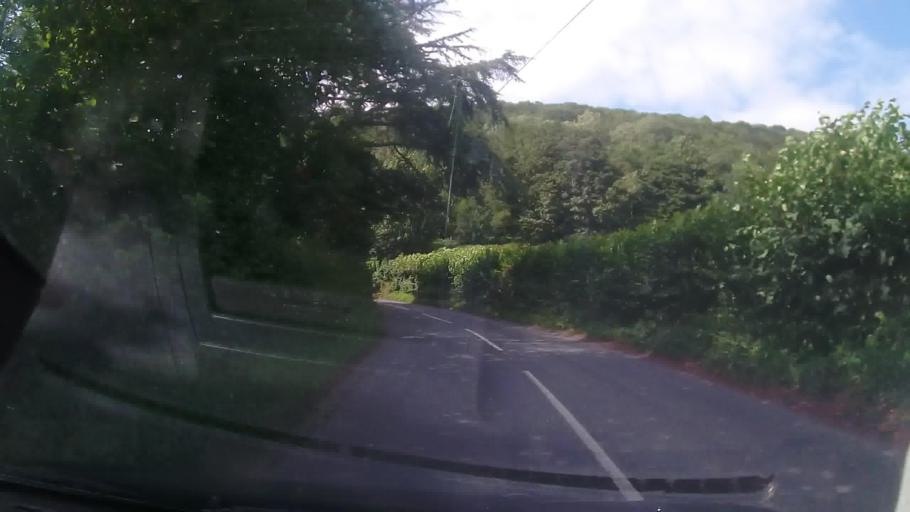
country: GB
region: Wales
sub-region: Sir Powys
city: Knighton
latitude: 52.3512
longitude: -3.0276
